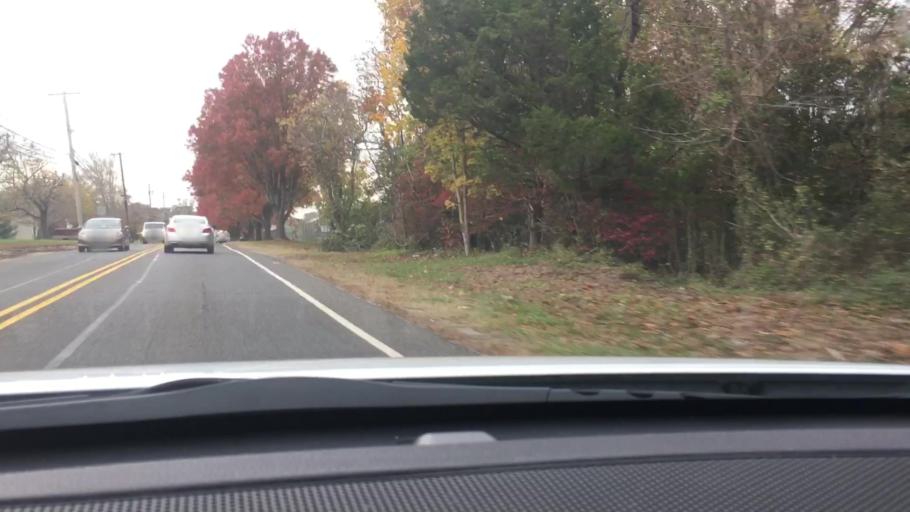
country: US
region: New Jersey
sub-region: Atlantic County
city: Northfield
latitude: 39.3900
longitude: -74.5495
